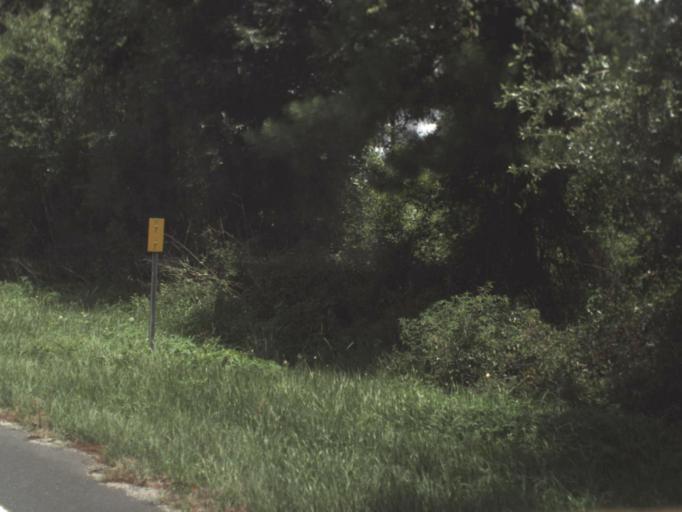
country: US
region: Florida
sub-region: Clay County
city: Keystone Heights
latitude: 29.6869
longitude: -82.0373
